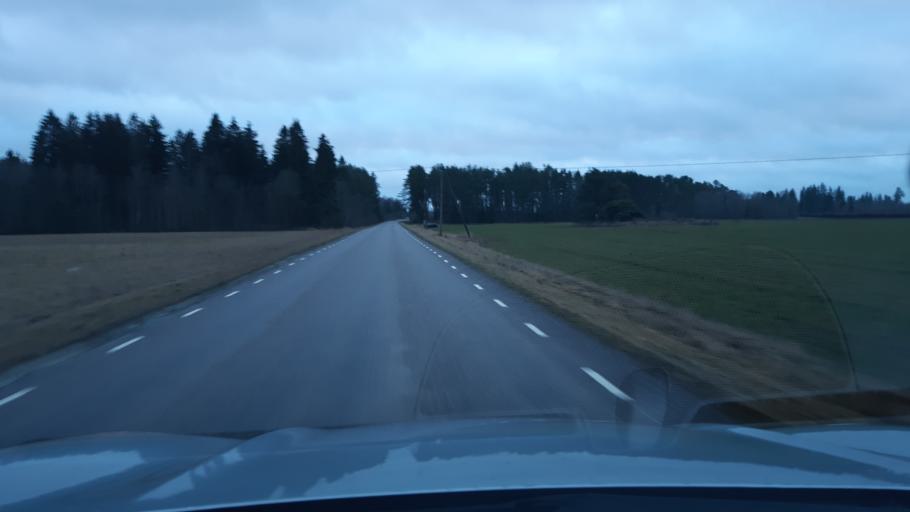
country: EE
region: Raplamaa
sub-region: Kohila vald
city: Kohila
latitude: 59.0762
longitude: 24.6795
